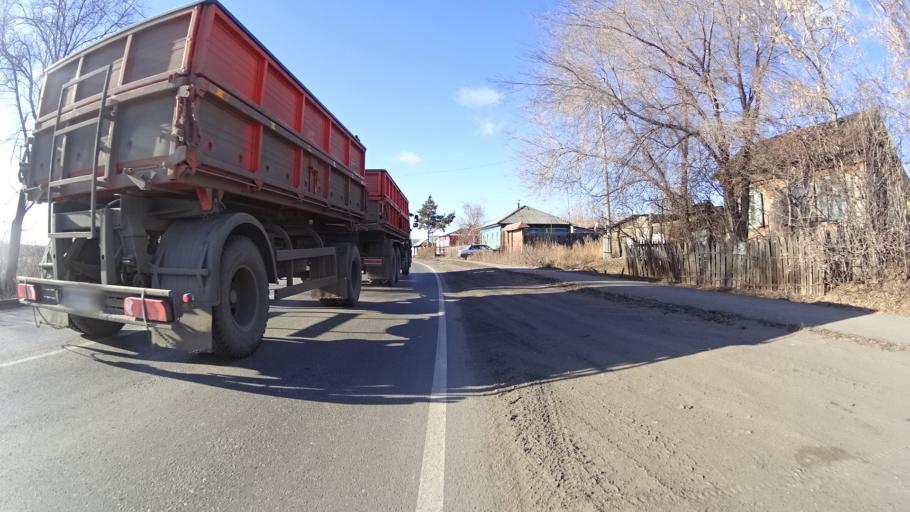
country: RU
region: Chelyabinsk
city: Troitsk
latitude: 54.0978
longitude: 61.5492
